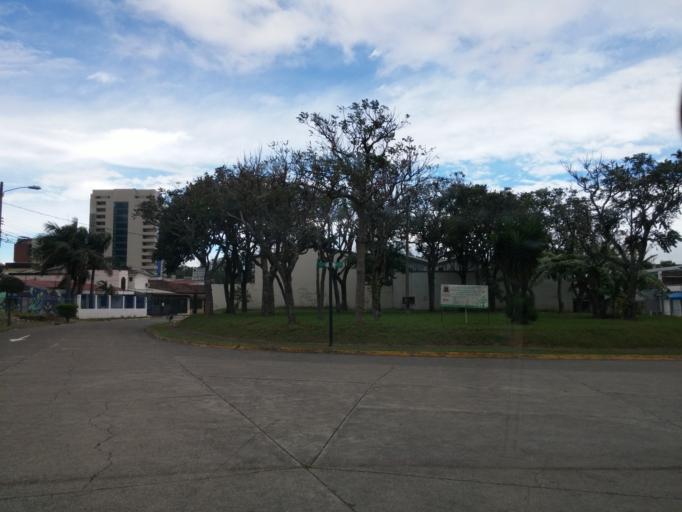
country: CR
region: San Jose
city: San Jose
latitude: 9.9305
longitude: -84.1077
